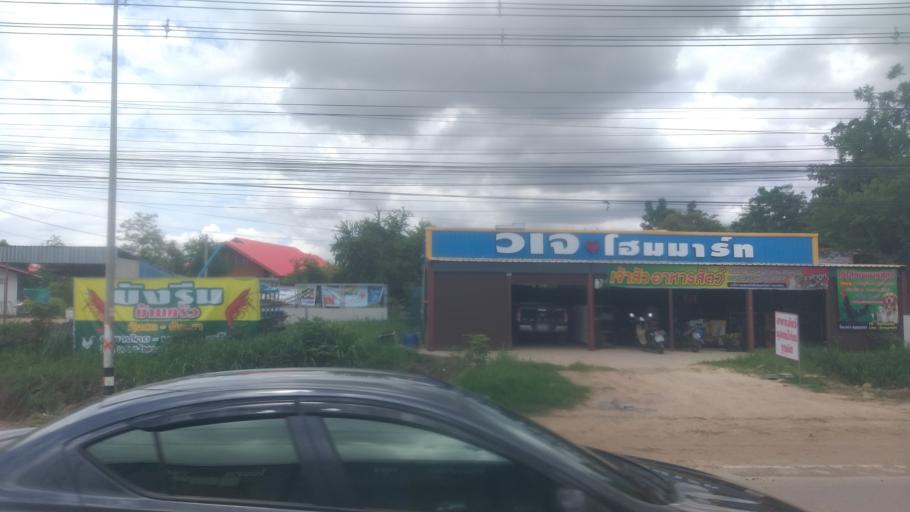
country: TH
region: Nakhon Ratchasima
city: Nakhon Ratchasima
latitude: 15.0657
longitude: 102.1219
